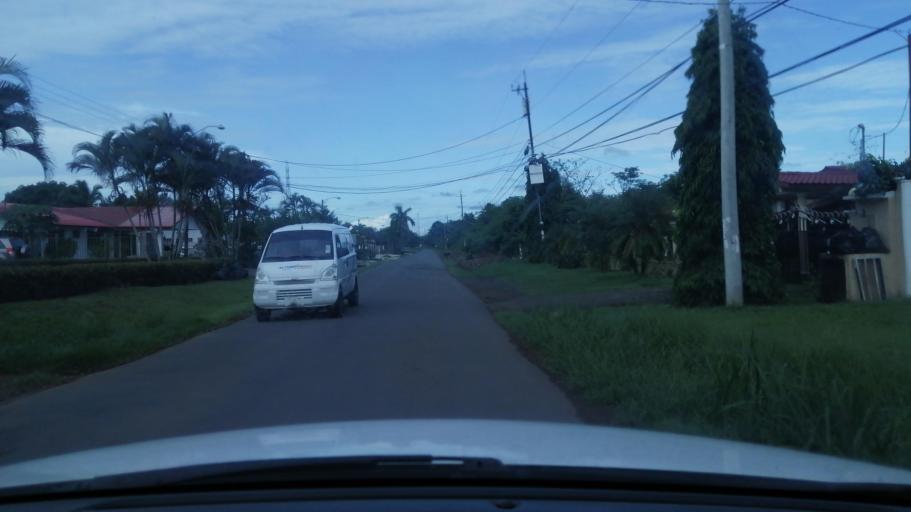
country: PA
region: Chiriqui
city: El Quiteno
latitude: 8.4672
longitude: -82.4139
